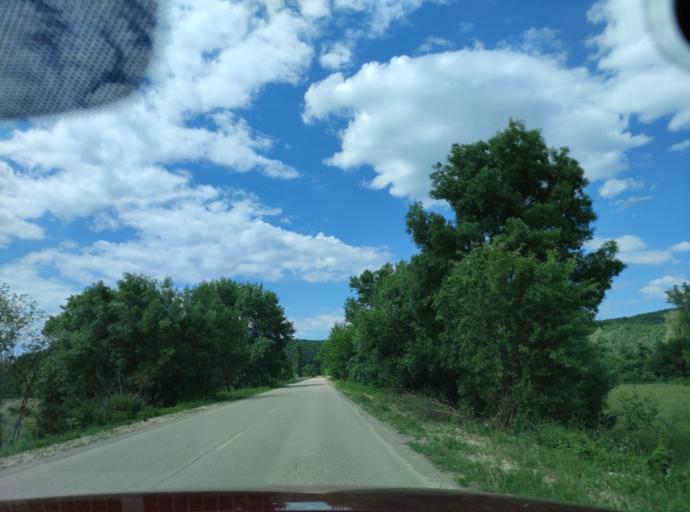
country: BG
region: Montana
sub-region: Obshtina Montana
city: Montana
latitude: 43.3981
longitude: 23.0722
